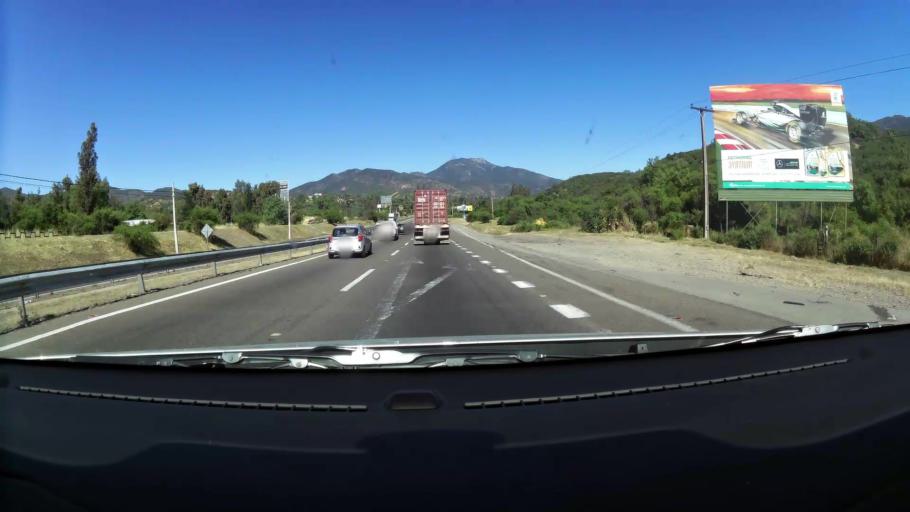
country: CL
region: Santiago Metropolitan
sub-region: Provincia de Melipilla
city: Melipilla
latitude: -33.4053
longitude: -71.1992
